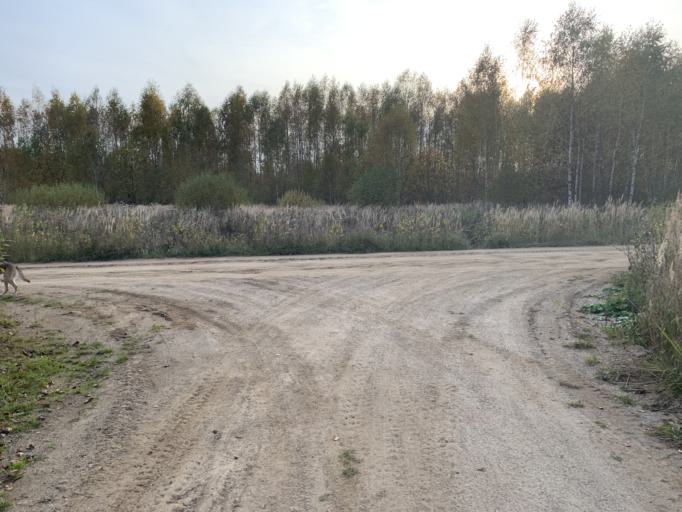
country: RU
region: Jaroslavl
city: Petrovsk
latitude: 56.9815
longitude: 39.3738
